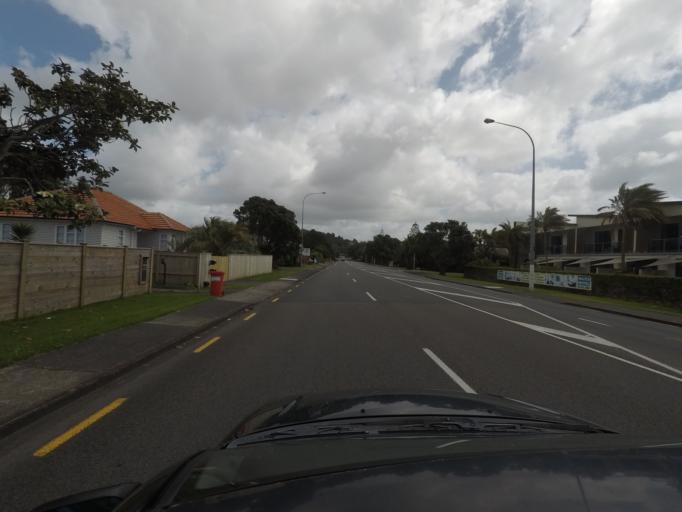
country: NZ
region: Auckland
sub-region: Auckland
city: Rothesay Bay
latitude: -36.5805
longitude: 174.6928
